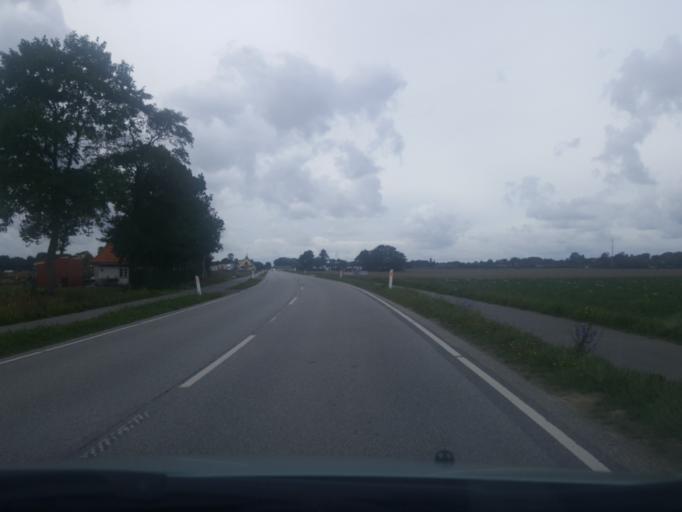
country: DK
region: Zealand
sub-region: Guldborgsund Kommune
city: Nykobing Falster
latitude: 54.7012
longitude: 11.9420
